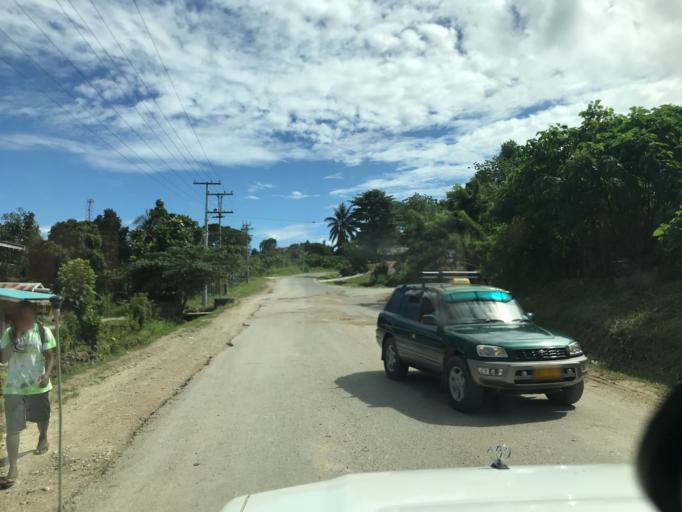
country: SB
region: Malaita
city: Auki
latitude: -8.7656
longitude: 160.6962
